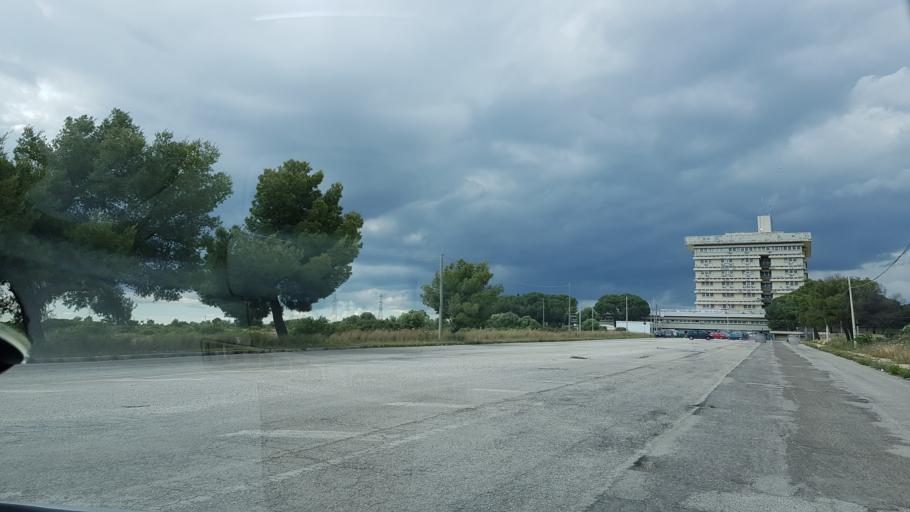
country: IT
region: Apulia
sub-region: Provincia di Taranto
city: Paolo VI
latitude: 40.5366
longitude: 17.2770
